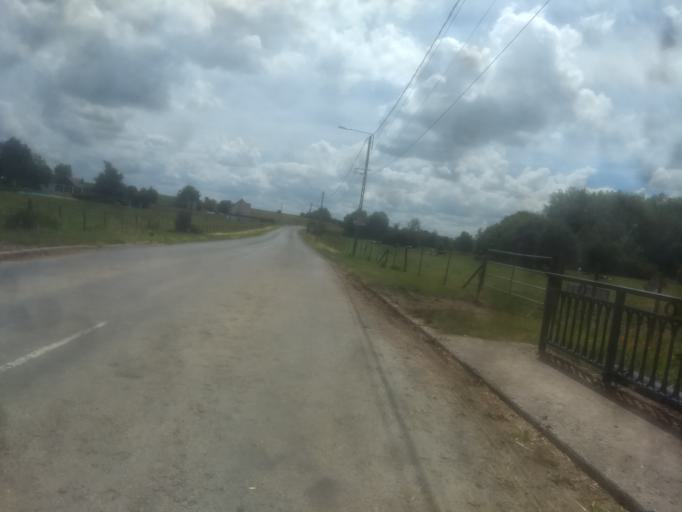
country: FR
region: Nord-Pas-de-Calais
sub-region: Departement du Pas-de-Calais
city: Mont-Saint-Eloi
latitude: 50.3459
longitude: 2.6513
